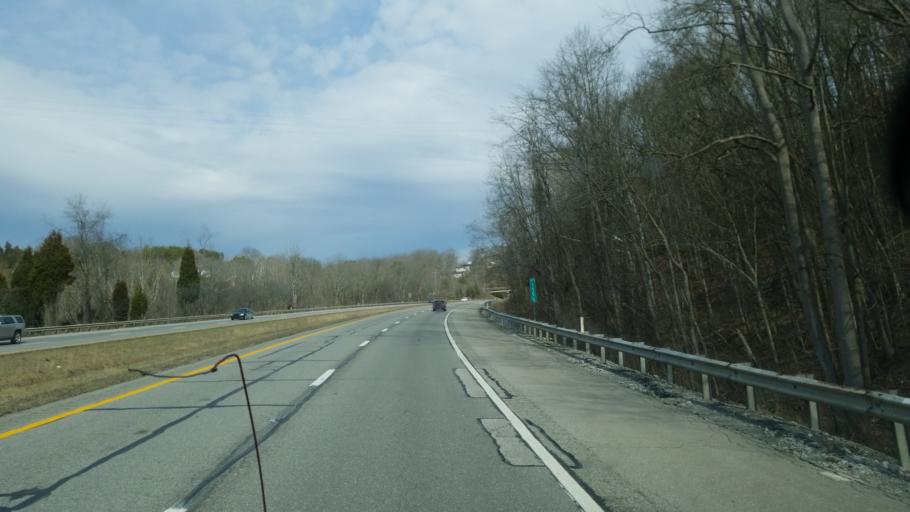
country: US
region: West Virginia
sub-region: Kanawha County
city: Sissonville
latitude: 38.5335
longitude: -81.6452
